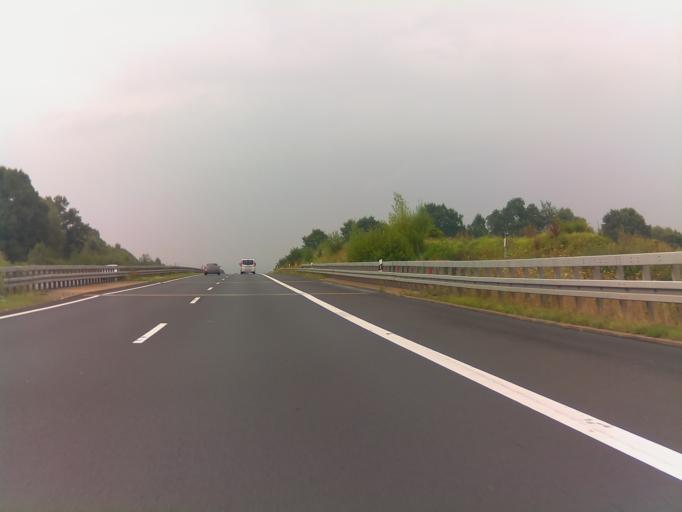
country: DE
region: Hesse
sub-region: Regierungsbezirk Kassel
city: Flieden
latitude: 50.4287
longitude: 9.5876
